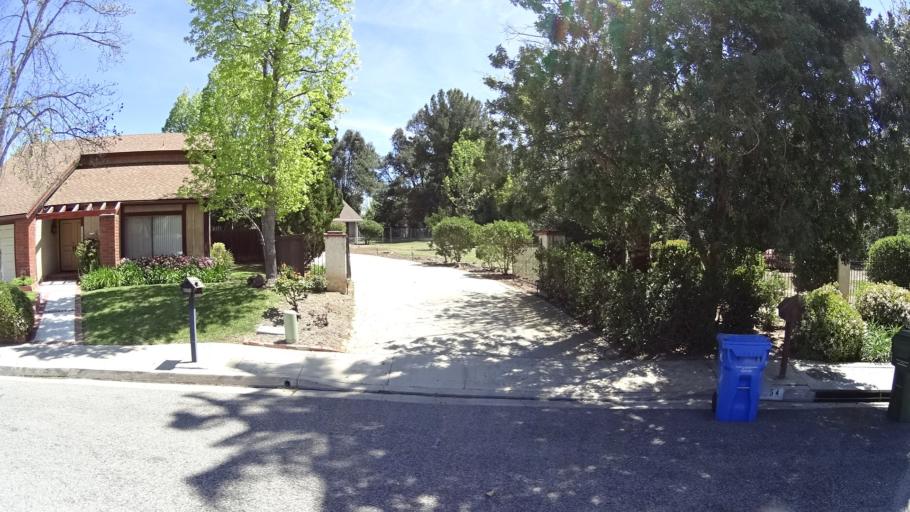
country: US
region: California
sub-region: Ventura County
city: Thousand Oaks
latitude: 34.2153
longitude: -118.8677
